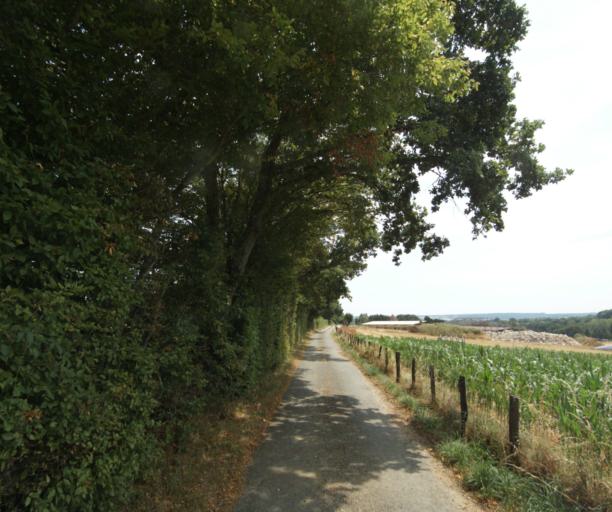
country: FR
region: Bourgogne
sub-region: Departement de Saone-et-Loire
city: Gueugnon
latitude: 46.5919
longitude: 4.0209
